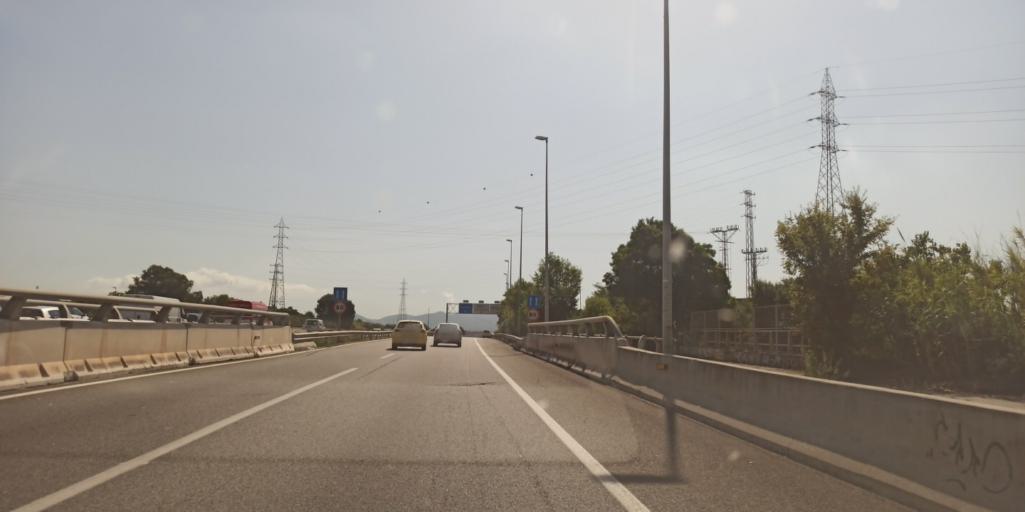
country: ES
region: Catalonia
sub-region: Provincia de Barcelona
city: Barbera del Valles
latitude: 41.5053
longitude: 2.1297
